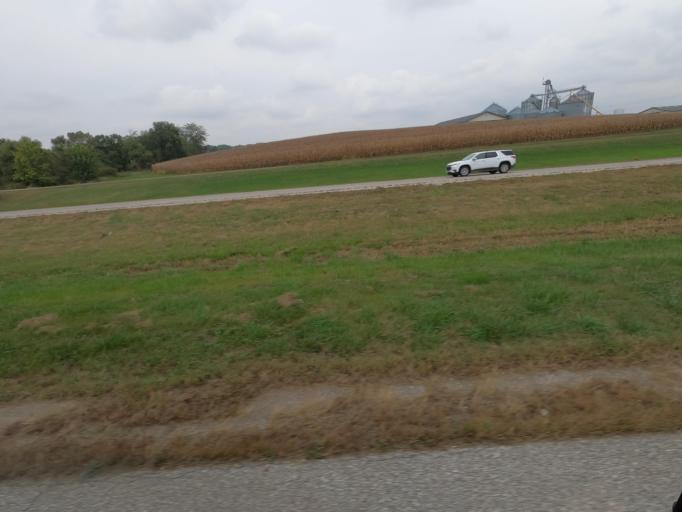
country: US
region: Iowa
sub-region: Wapello County
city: Eddyville
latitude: 41.1429
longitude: -92.6138
